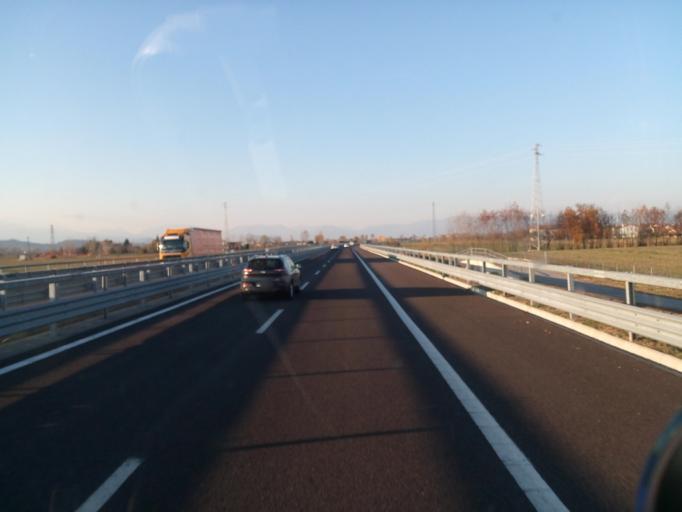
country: IT
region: Veneto
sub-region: Provincia di Vicenza
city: Longare
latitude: 45.4922
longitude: 11.6203
